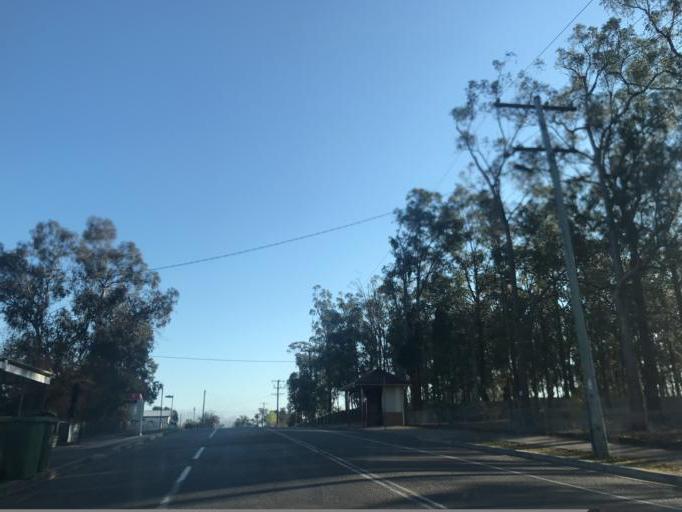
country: AU
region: New South Wales
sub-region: Cessnock
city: Cessnock
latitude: -32.9145
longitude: 151.3107
